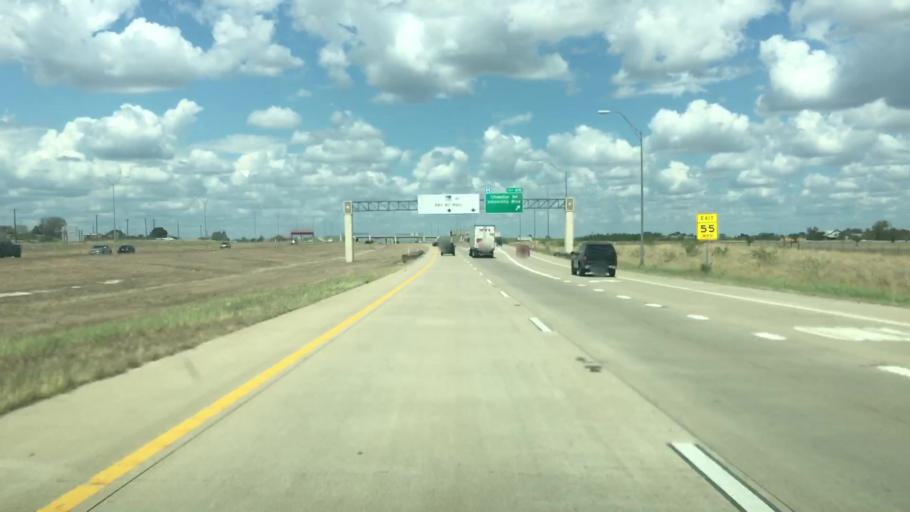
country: US
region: Texas
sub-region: Williamson County
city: Hutto
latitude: 30.5801
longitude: -97.5863
